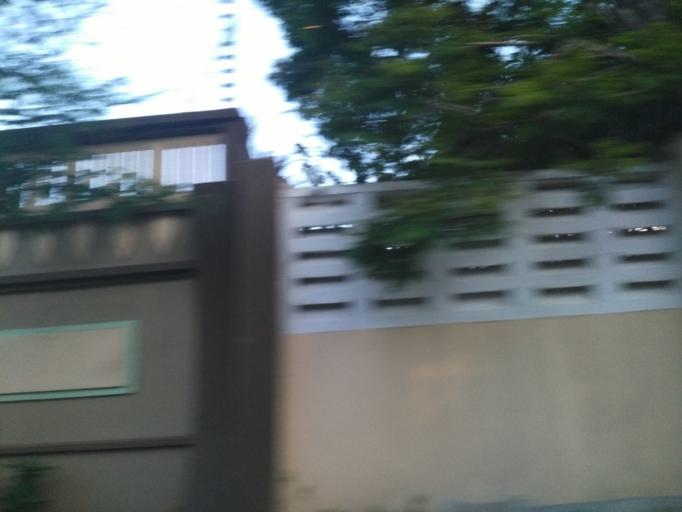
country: TZ
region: Dar es Salaam
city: Magomeni
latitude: -6.7797
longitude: 39.2832
